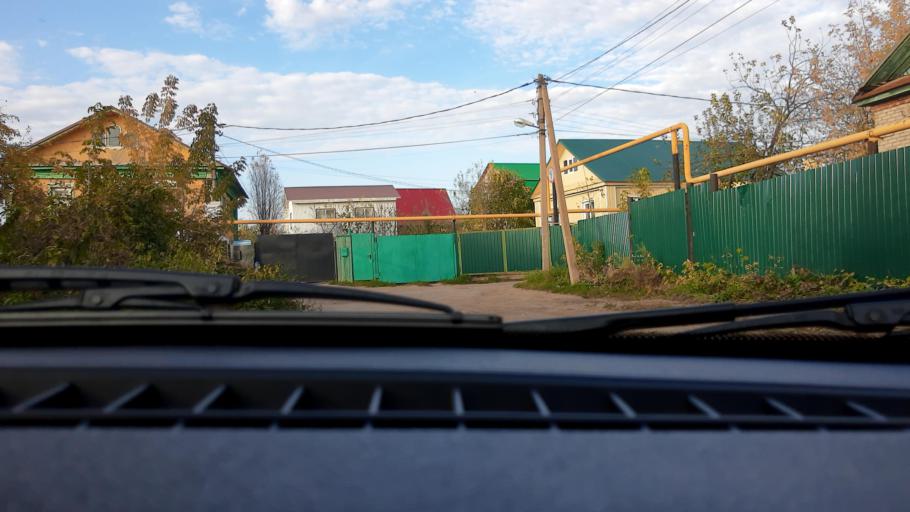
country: RU
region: Bashkortostan
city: Ufa
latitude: 54.7331
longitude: 55.8991
